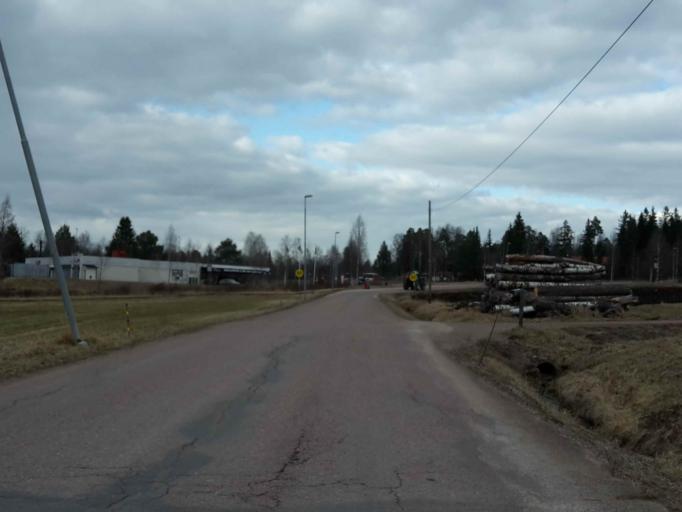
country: SE
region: Dalarna
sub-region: Orsa Kommun
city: Orsa
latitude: 61.1059
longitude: 14.6282
